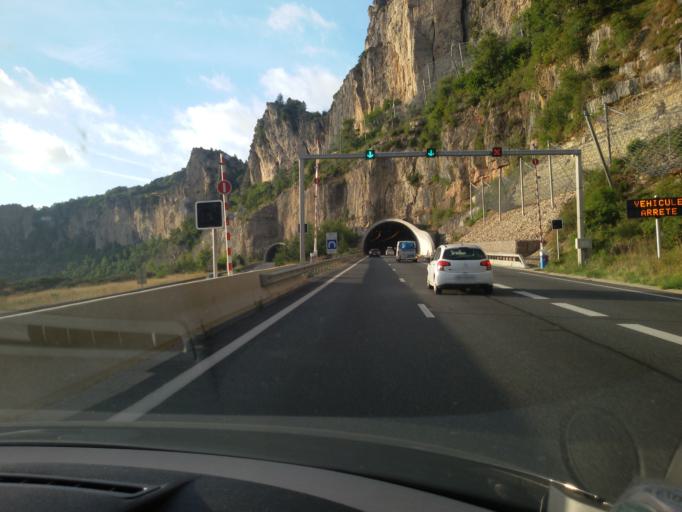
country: FR
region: Languedoc-Roussillon
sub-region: Departement de l'Herault
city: Lodeve
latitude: 43.8260
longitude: 3.3167
